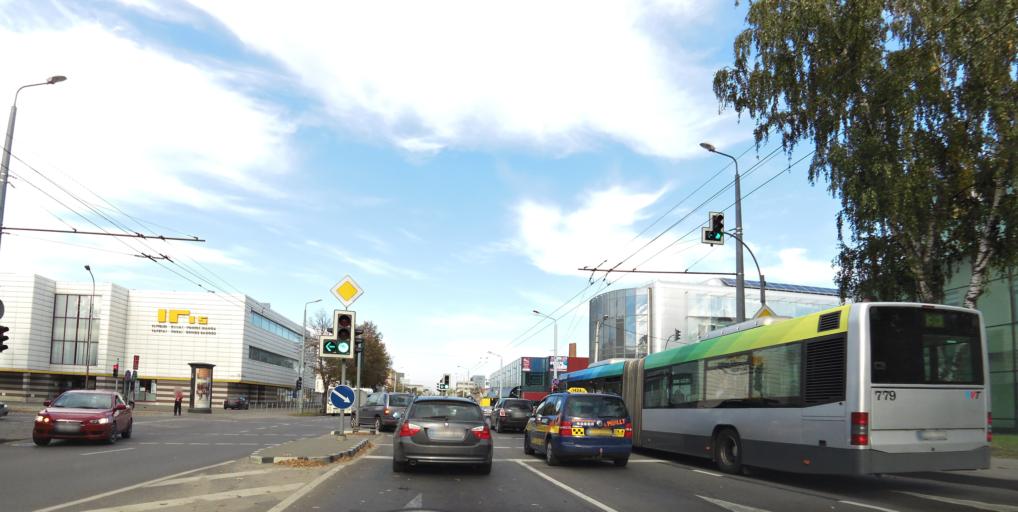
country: LT
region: Vilnius County
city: Naujamiestis
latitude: 54.6691
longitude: 25.2706
